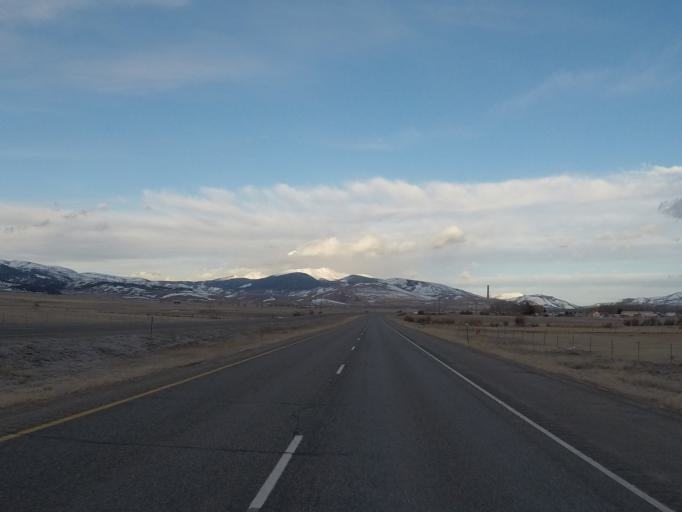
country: US
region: Montana
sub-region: Deer Lodge County
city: Warm Springs
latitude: 46.0958
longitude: -112.8164
